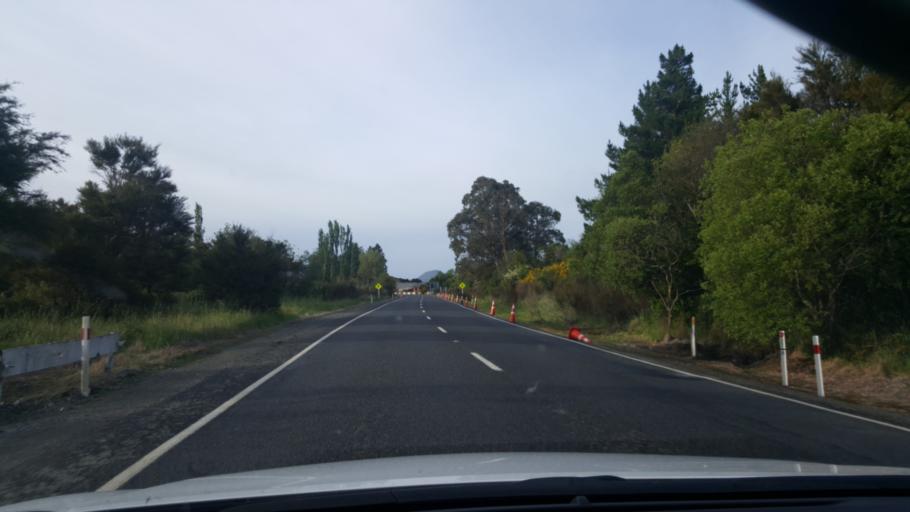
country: NZ
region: Waikato
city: Turangi
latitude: -38.9739
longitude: 175.7705
